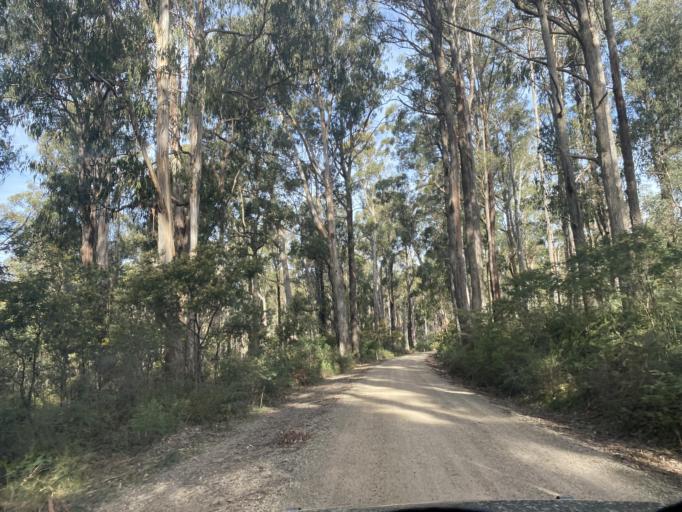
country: AU
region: Victoria
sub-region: Mansfield
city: Mansfield
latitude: -36.8494
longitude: 146.1831
